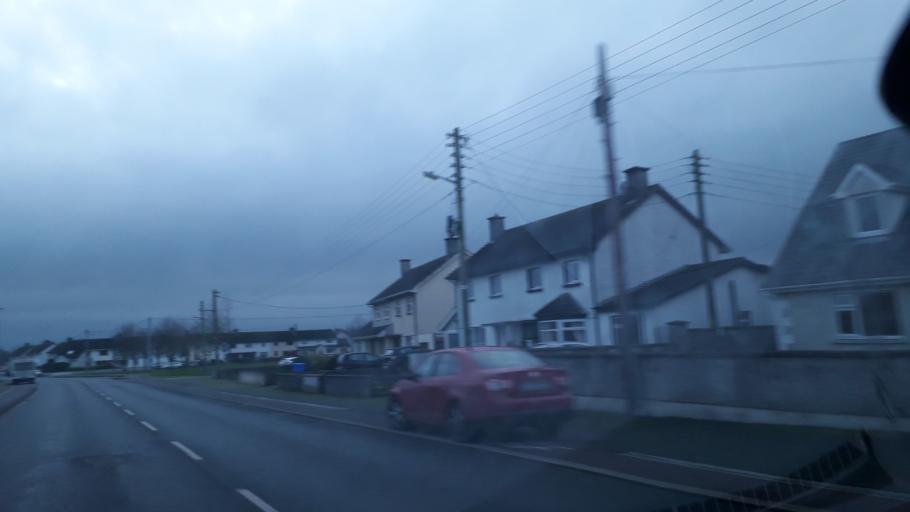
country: IE
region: Leinster
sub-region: Kilkenny
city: Kilkenny
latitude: 52.6647
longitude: -7.2403
